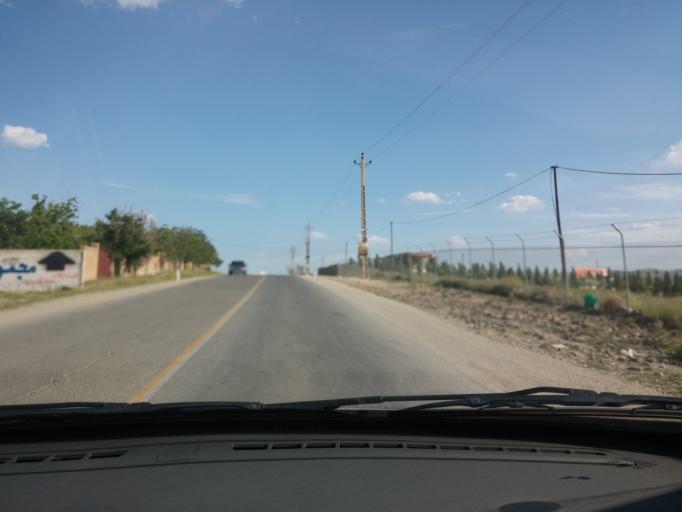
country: IR
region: Tehran
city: Damavand
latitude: 35.6643
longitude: 52.0723
